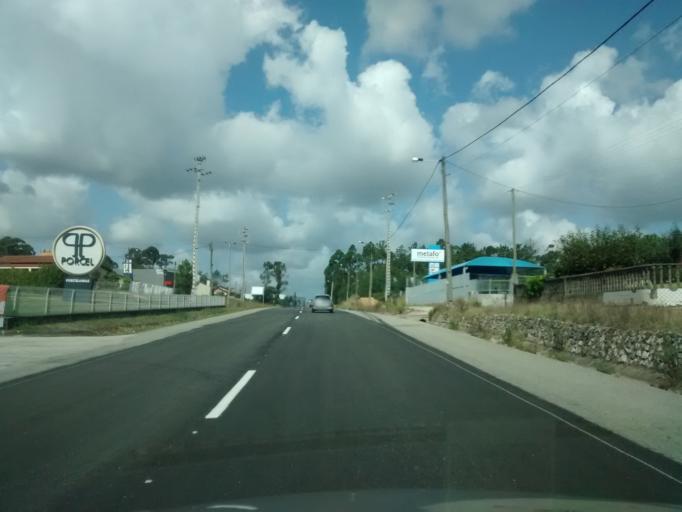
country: PT
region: Aveiro
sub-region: Oliveira do Bairro
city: Oia
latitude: 40.5373
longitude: -8.5200
